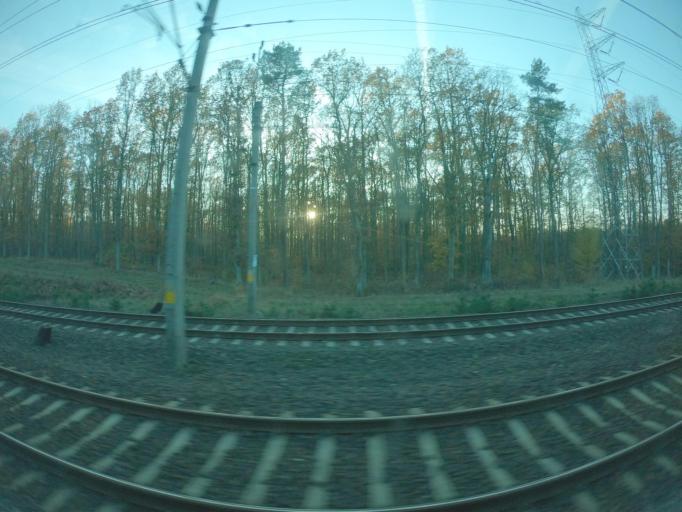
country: PL
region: Lubusz
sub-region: Powiat slubicki
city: Rzepin
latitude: 52.3204
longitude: 14.8509
